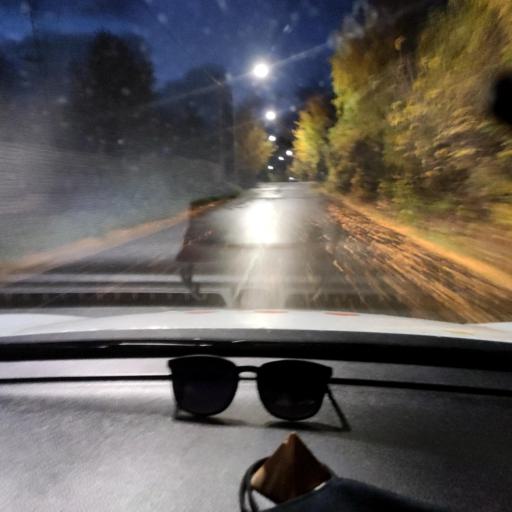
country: RU
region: Tatarstan
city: Verkhniy Uslon
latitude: 55.6049
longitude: 49.0204
